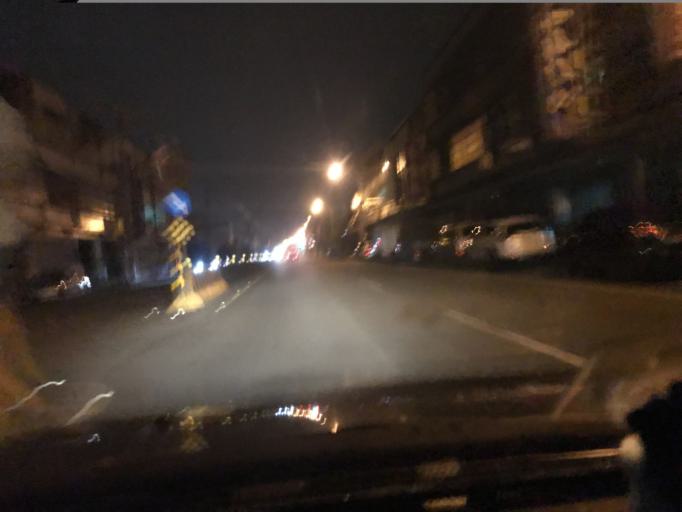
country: TW
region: Taiwan
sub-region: Hsinchu
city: Zhubei
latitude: 24.7865
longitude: 121.0654
